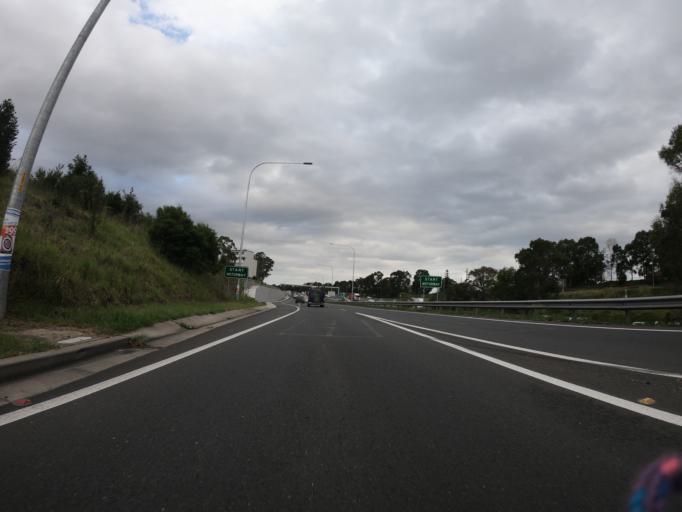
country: AU
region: New South Wales
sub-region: Holroyd
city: Merrylands
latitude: -33.8160
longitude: 150.9646
